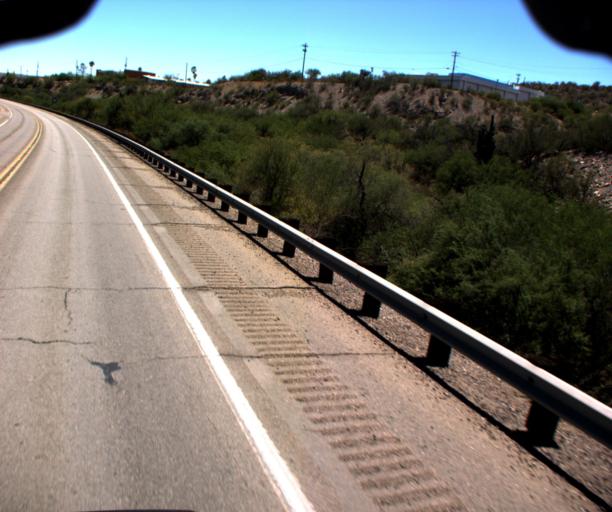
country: US
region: Arizona
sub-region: Pinal County
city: Kearny
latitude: 32.9966
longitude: -110.7692
